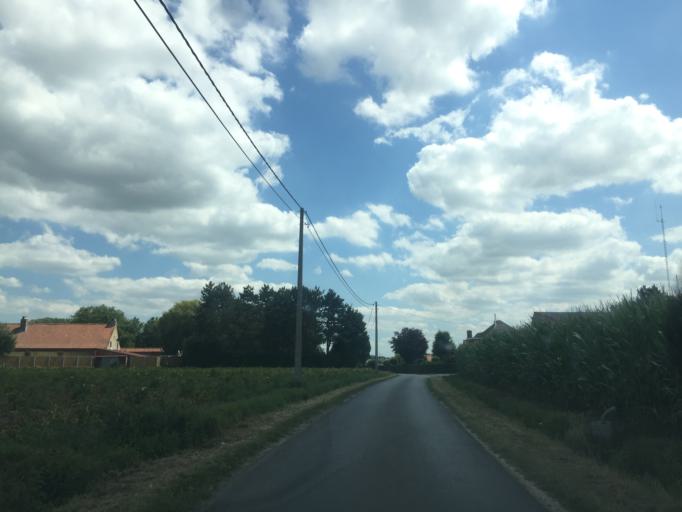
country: BE
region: Flanders
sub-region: Provincie West-Vlaanderen
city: Staden
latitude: 50.9528
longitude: 2.9898
